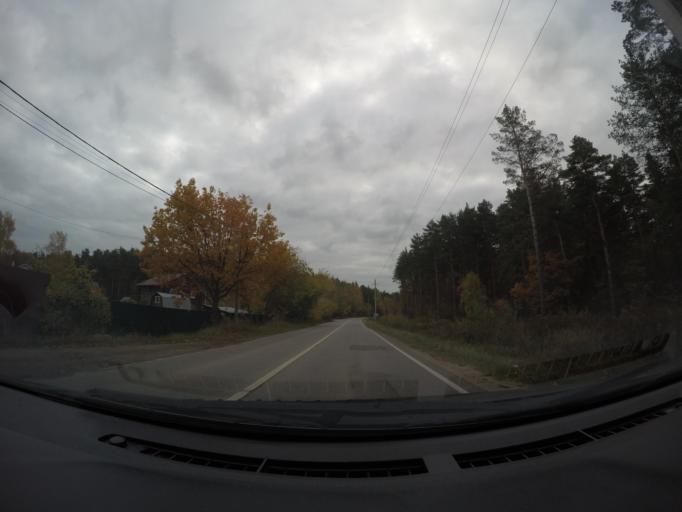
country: RU
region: Moskovskaya
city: Gzhel'
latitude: 55.6383
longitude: 38.4163
